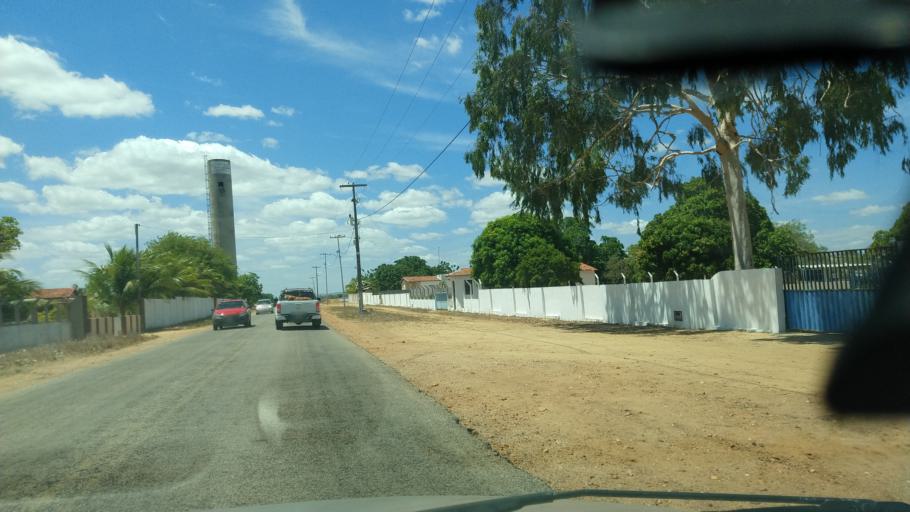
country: BR
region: Rio Grande do Norte
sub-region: Sao Paulo Do Potengi
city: Sao Paulo do Potengi
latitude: -5.9158
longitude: -35.7282
